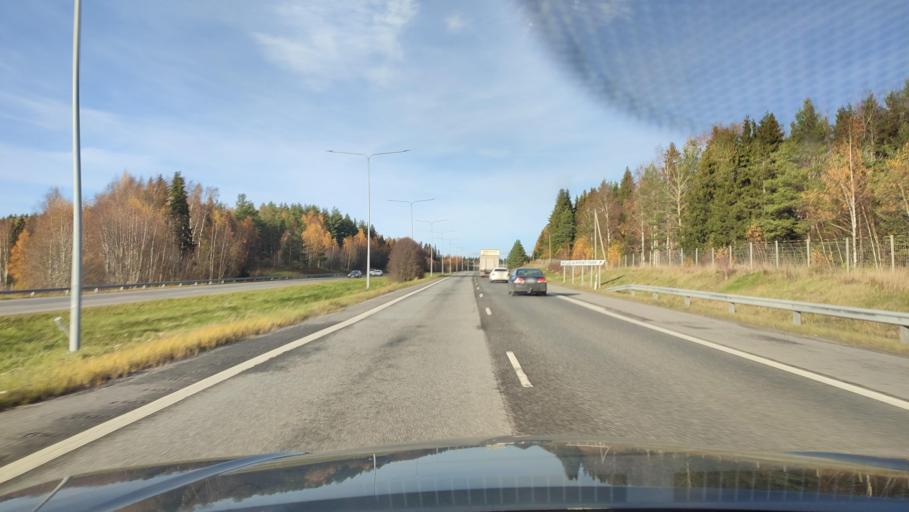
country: FI
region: Ostrobothnia
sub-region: Vaasa
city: Ristinummi
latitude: 63.0484
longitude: 21.7204
